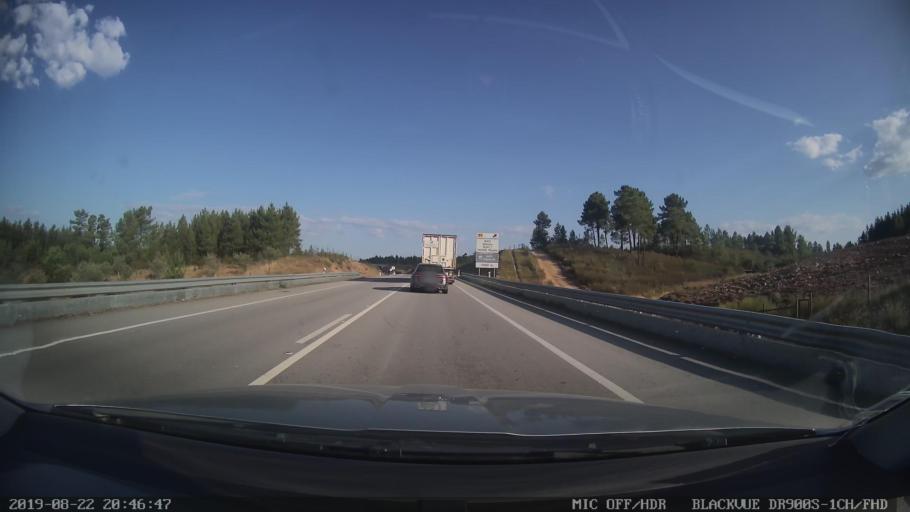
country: PT
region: Castelo Branco
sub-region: Proenca-A-Nova
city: Proenca-a-Nova
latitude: 39.7294
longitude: -7.8794
